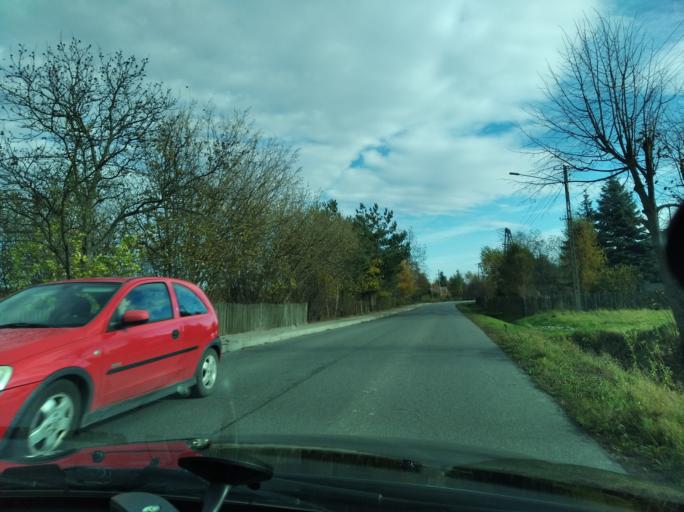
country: PL
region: Subcarpathian Voivodeship
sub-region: Powiat debicki
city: Brzeznica
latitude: 50.0963
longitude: 21.5361
